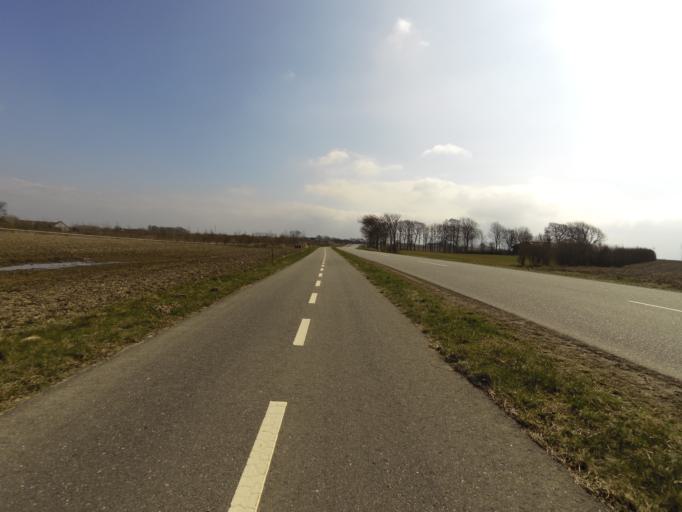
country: DK
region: Central Jutland
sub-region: Struer Kommune
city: Struer
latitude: 56.4477
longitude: 8.6232
